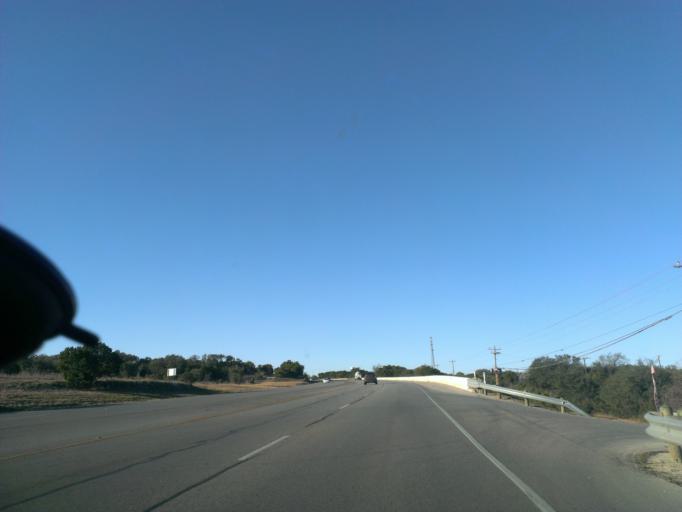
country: US
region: Texas
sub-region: Travis County
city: Bee Cave
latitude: 30.2183
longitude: -97.9618
